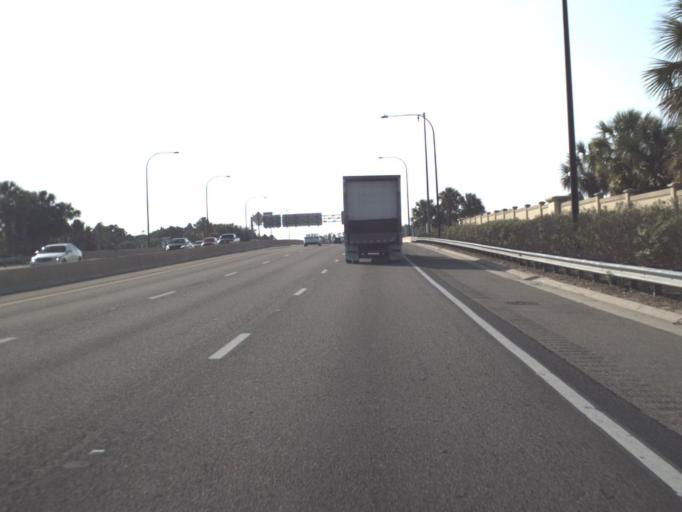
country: US
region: Florida
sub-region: Orange County
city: Orlando
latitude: 28.5417
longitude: -81.4123
